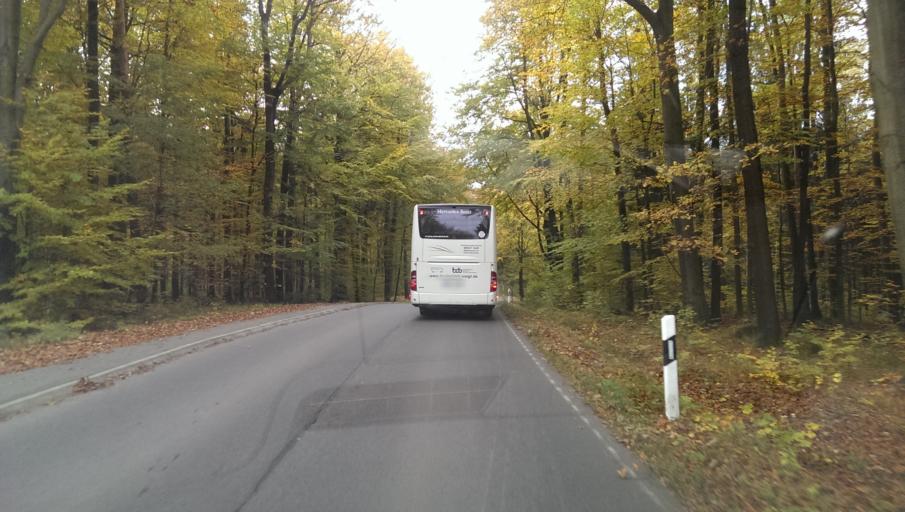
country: DE
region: Saxony
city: Stadt Wehlen
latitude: 50.9728
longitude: 14.0627
